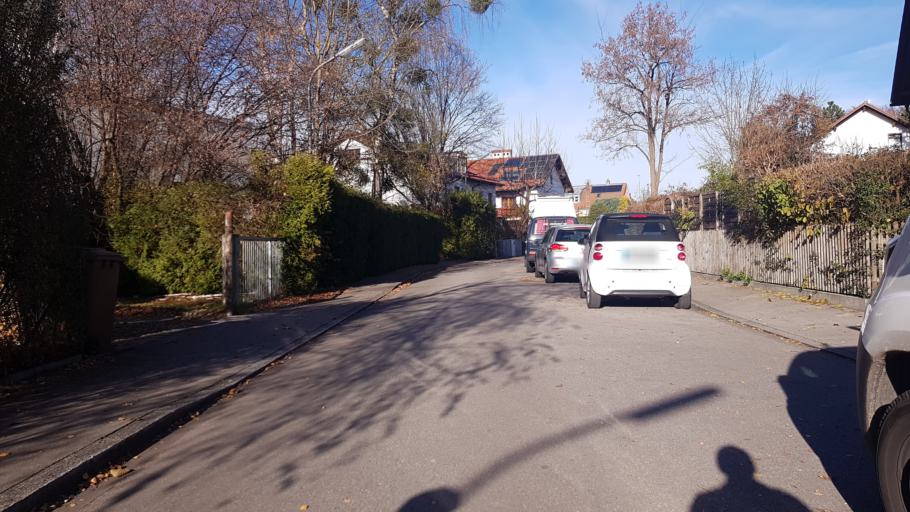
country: DE
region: Bavaria
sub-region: Upper Bavaria
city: Karlsfeld
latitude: 48.1980
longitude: 11.5121
